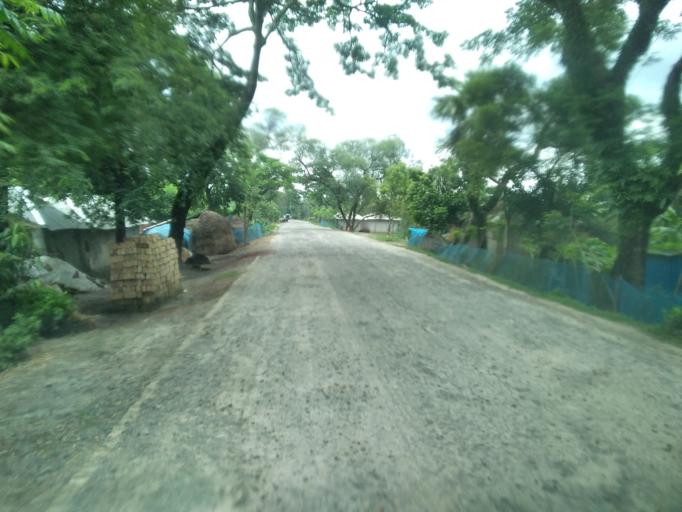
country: IN
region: West Bengal
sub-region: North 24 Parganas
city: Gosaba
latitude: 22.2677
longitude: 89.1641
